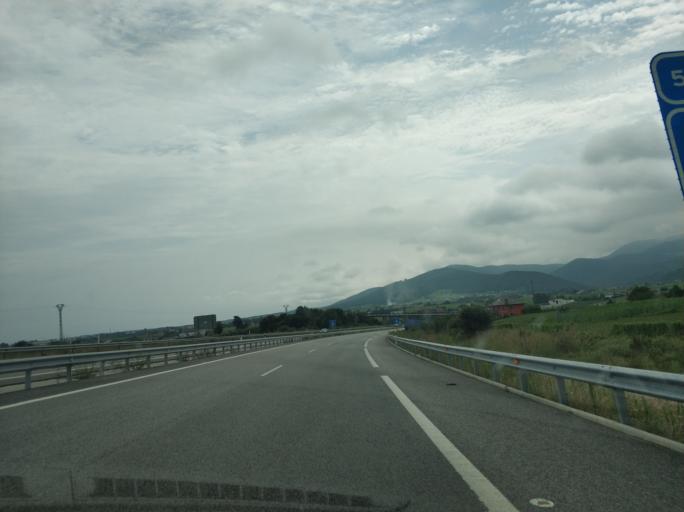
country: ES
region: Asturias
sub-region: Province of Asturias
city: Navia
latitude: 43.5294
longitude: -6.5644
